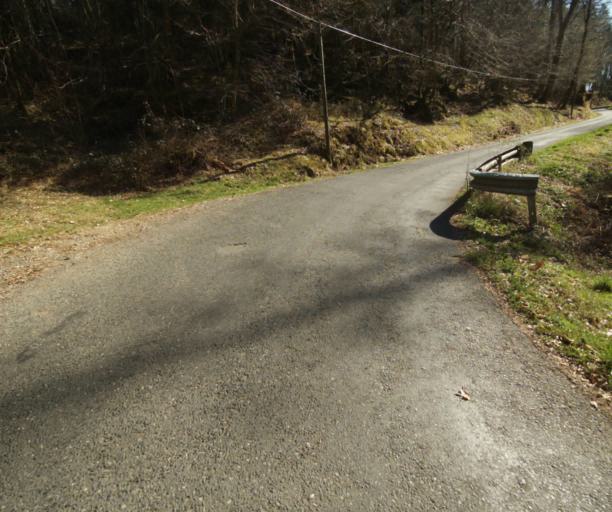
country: FR
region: Limousin
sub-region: Departement de la Correze
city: Tulle
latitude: 45.2821
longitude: 1.7365
